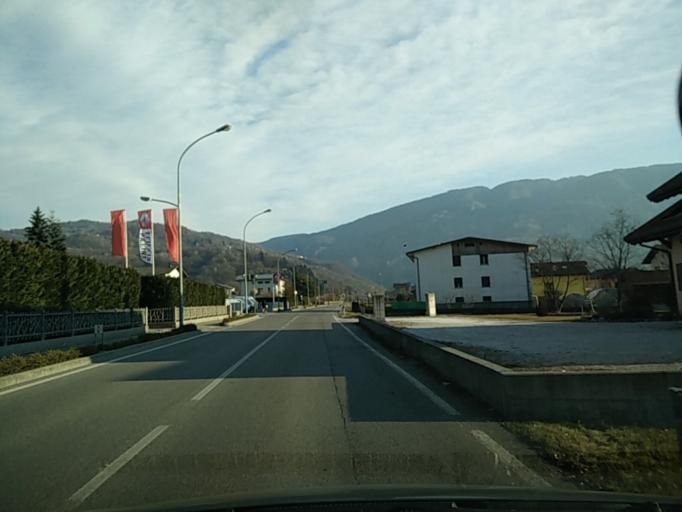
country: IT
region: Veneto
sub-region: Provincia di Belluno
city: Farra d'Alpago
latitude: 46.1300
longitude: 12.3466
